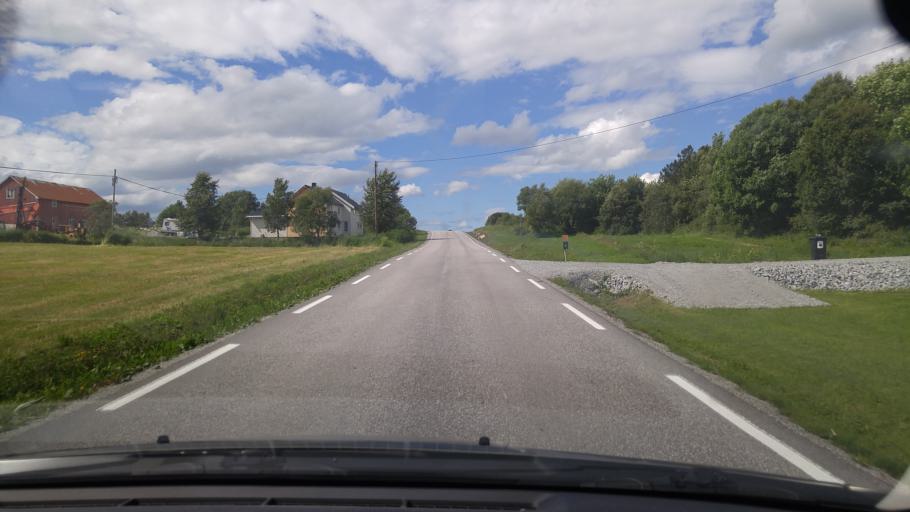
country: NO
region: Nord-Trondelag
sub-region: Vikna
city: Rorvik
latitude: 64.9188
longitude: 11.2164
